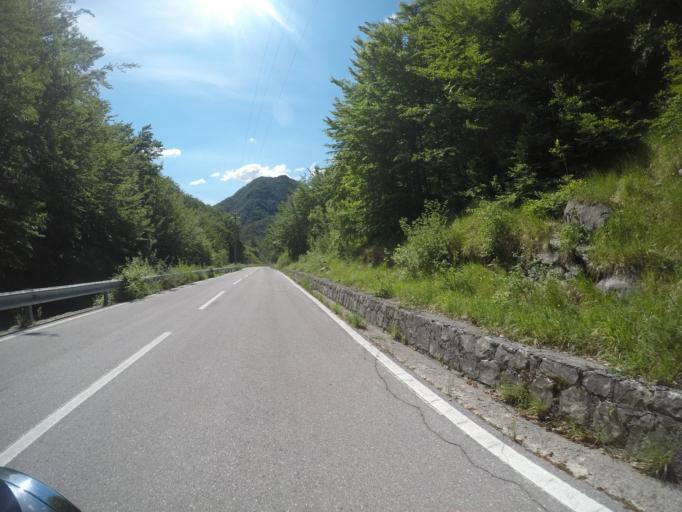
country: IT
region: Tuscany
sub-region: Provincia di Lucca
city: Seravezza
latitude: 44.0614
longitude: 10.2359
